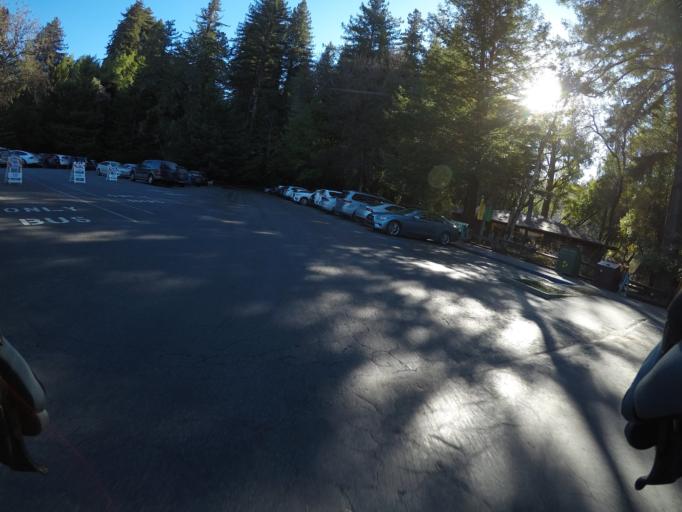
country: US
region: California
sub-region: Santa Cruz County
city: Mount Hermon
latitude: 37.0403
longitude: -122.0638
